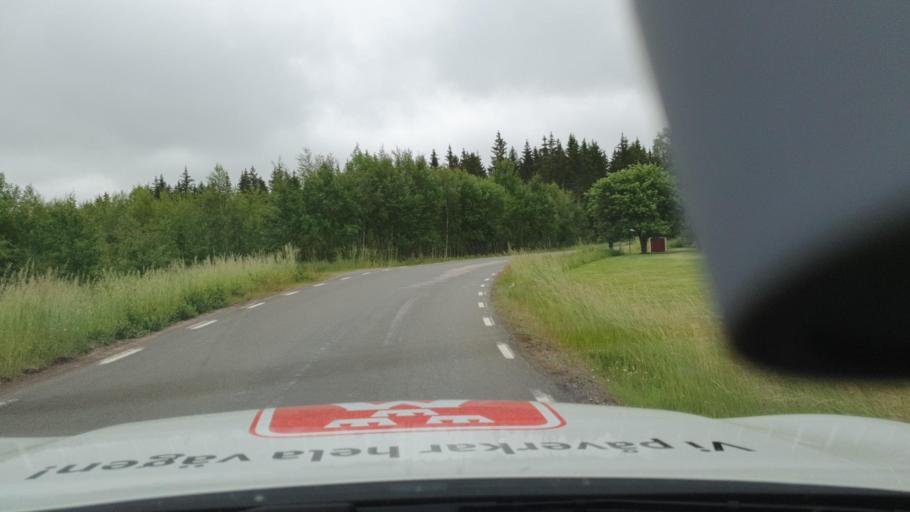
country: SE
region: Vaestra Goetaland
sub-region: Tidaholms Kommun
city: Olofstorp
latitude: 58.3809
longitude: 14.0012
